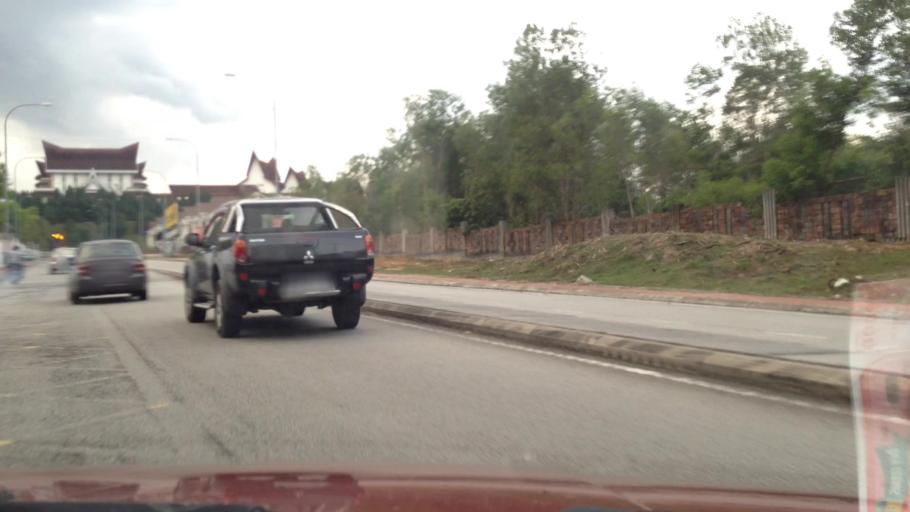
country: MY
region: Selangor
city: Shah Alam
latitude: 3.0723
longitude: 101.5394
